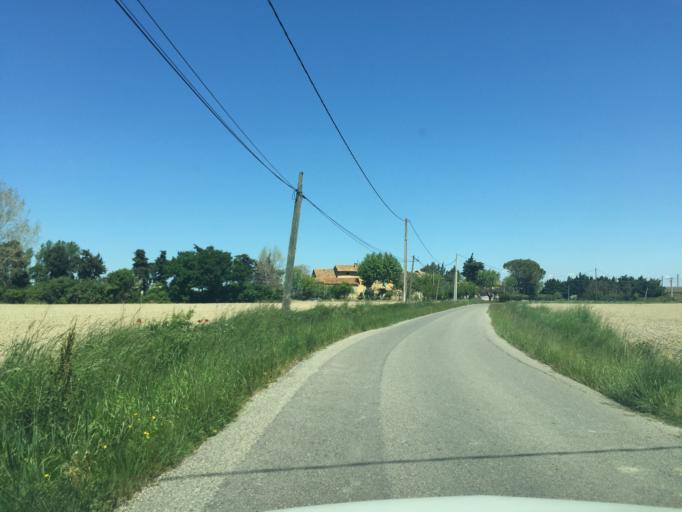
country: FR
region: Provence-Alpes-Cote d'Azur
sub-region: Departement du Vaucluse
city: Caderousse
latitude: 44.1072
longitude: 4.7713
